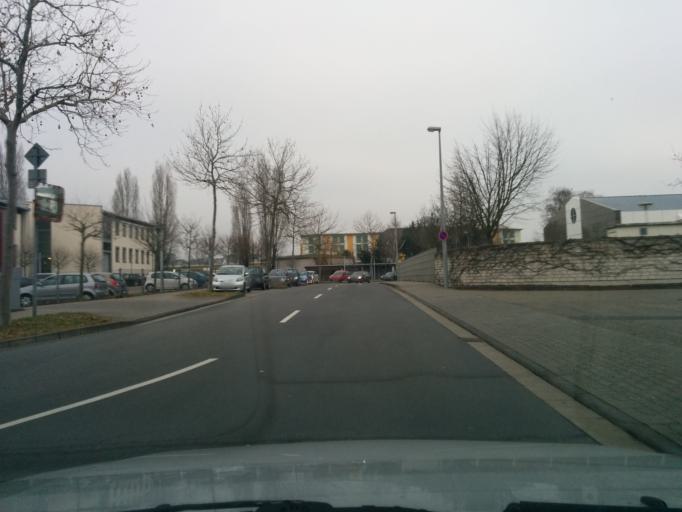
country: DE
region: Rheinland-Pfalz
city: Koblenz
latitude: 50.3644
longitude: 7.5775
